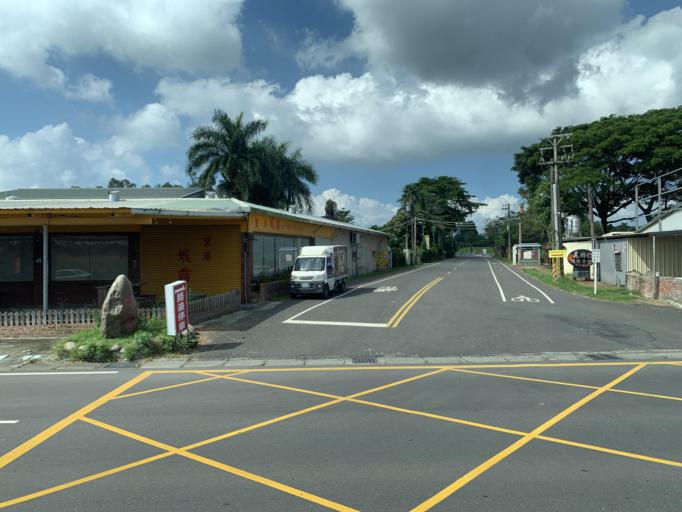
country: TW
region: Taiwan
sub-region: Pingtung
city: Pingtung
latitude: 22.8780
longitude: 120.4968
